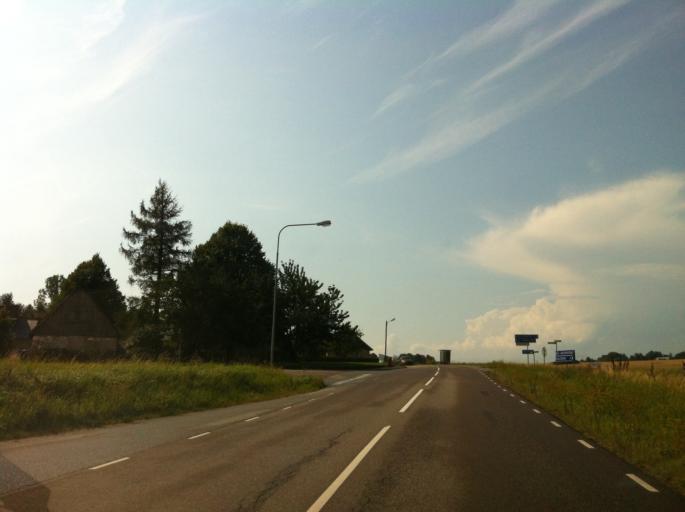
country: SE
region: Skane
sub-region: Helsingborg
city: Glumslov
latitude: 55.9386
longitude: 12.8512
